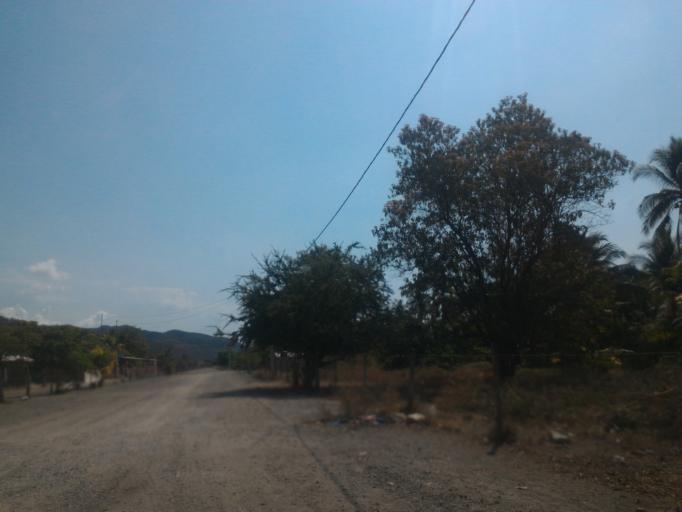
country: MX
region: Michoacan
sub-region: Coalcoman de Vazquez Pallares
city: Coalcoman de Vazquez Pallares
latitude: 18.2736
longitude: -103.3462
